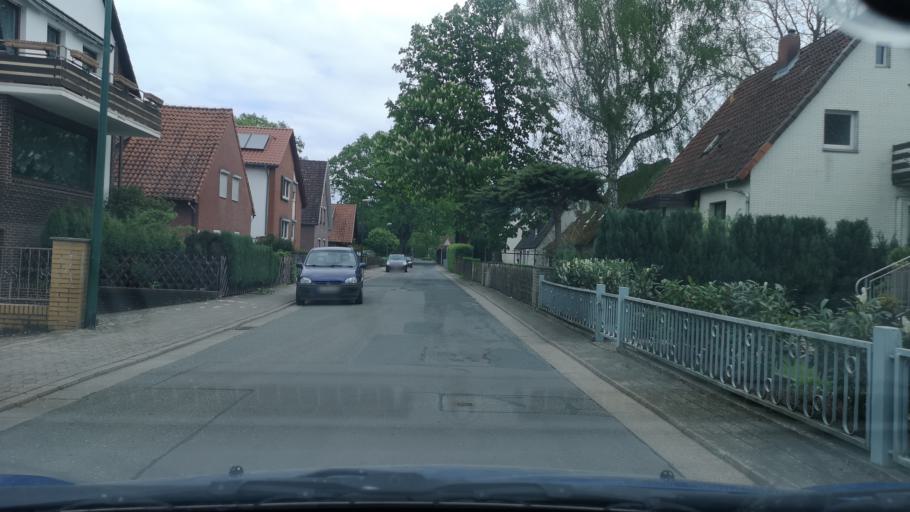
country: DE
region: Lower Saxony
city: Langenhagen
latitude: 52.4634
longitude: 9.7500
